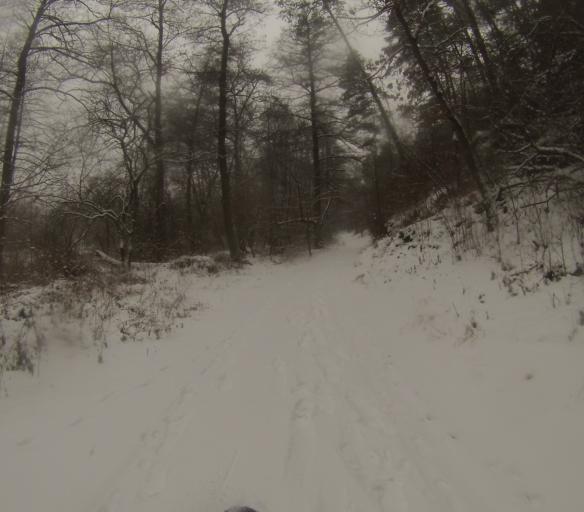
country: CZ
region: South Moravian
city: Orechov
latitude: 49.1283
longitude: 16.5432
